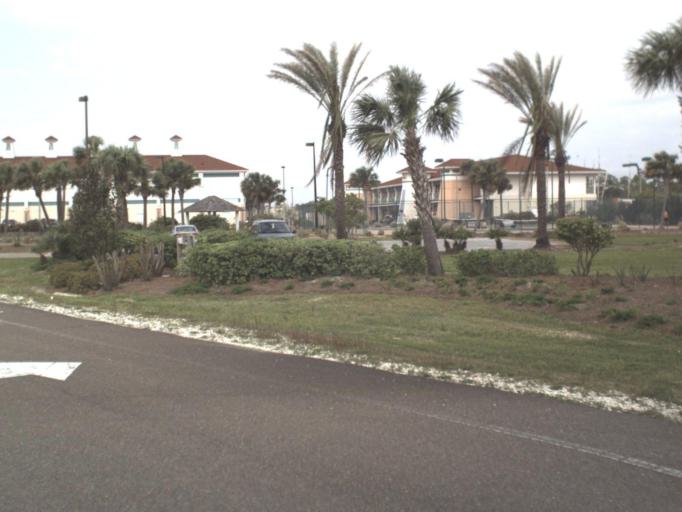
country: US
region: Alabama
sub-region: Baldwin County
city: Orange Beach
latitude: 30.2979
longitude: -87.4299
